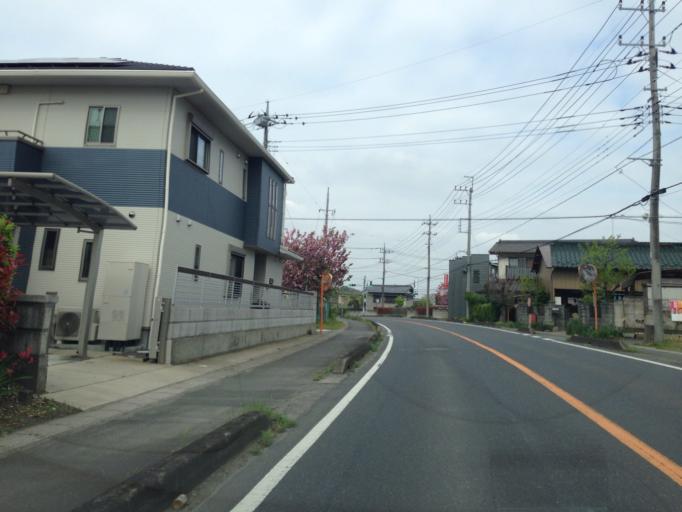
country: JP
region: Ibaraki
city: Ishige
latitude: 36.1577
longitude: 139.9625
